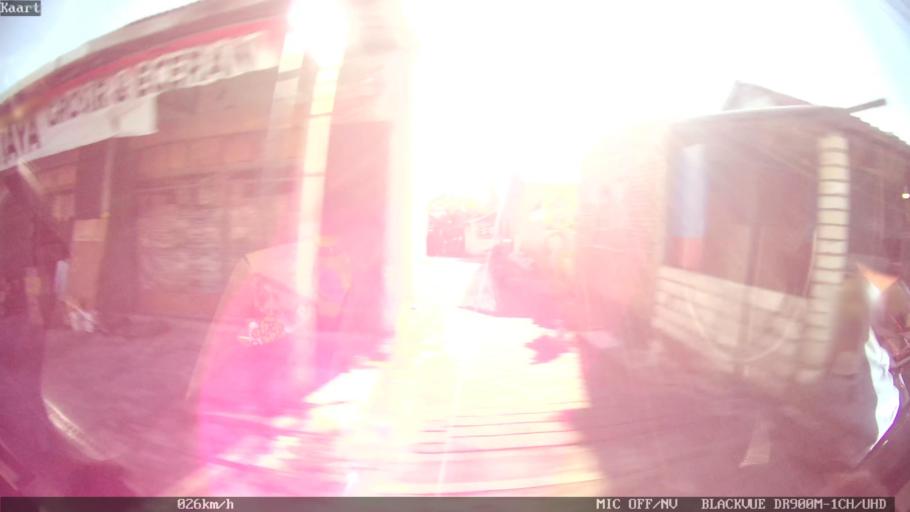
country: ID
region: Bali
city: Banjar Gunungpande
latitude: -8.6228
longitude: 115.1673
